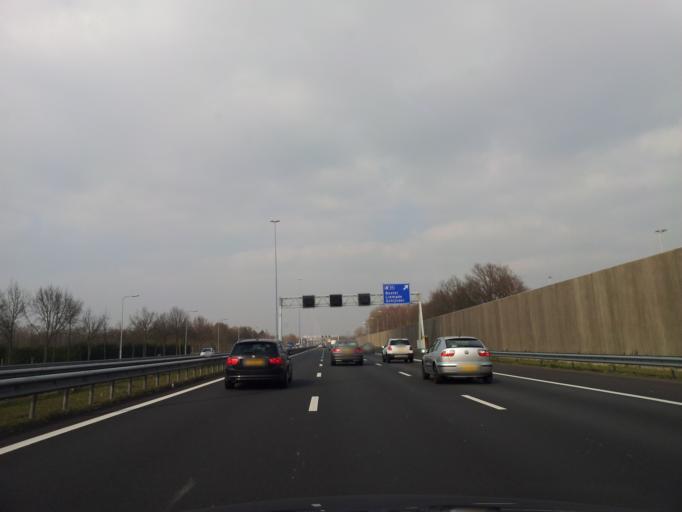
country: NL
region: North Brabant
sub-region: Gemeente Boxtel
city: Boxtel
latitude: 51.5702
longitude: 5.3565
